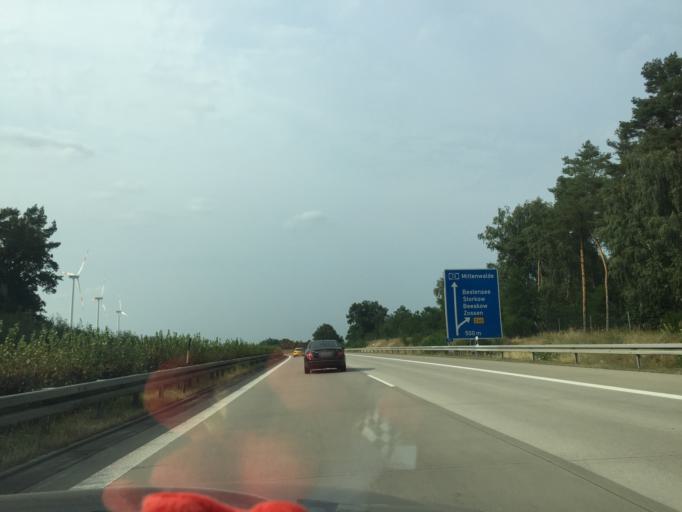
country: DE
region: Brandenburg
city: Mittenwalde
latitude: 52.2416
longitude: 13.5913
